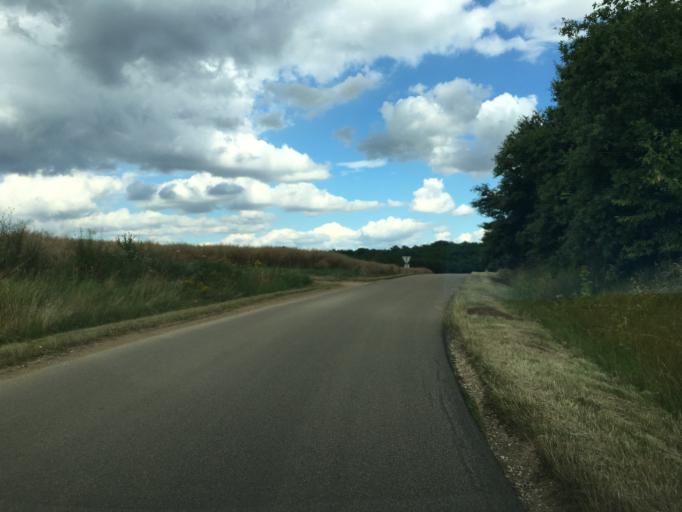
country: FR
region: Bourgogne
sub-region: Departement de l'Yonne
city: Charbuy
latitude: 47.8234
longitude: 3.4304
